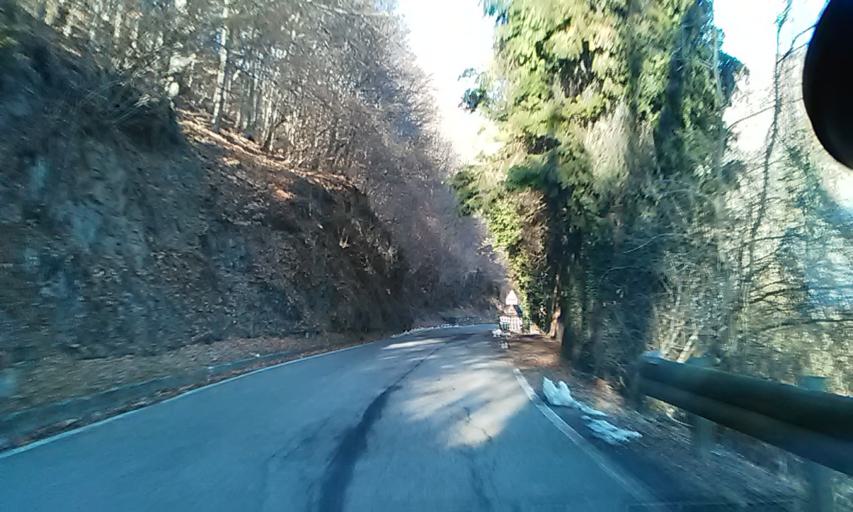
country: IT
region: Piedmont
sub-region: Provincia di Vercelli
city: Valduggia
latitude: 45.7507
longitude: 8.3410
